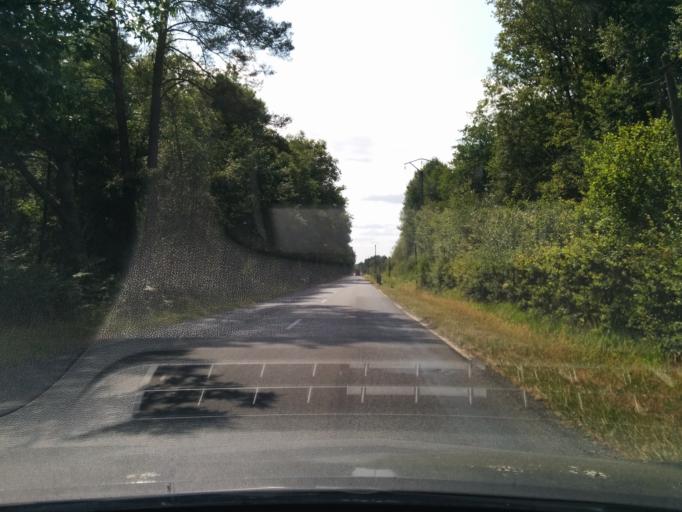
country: FR
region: Centre
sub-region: Departement du Cher
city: Neuvy-sur-Barangeon
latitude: 47.3212
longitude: 2.2845
